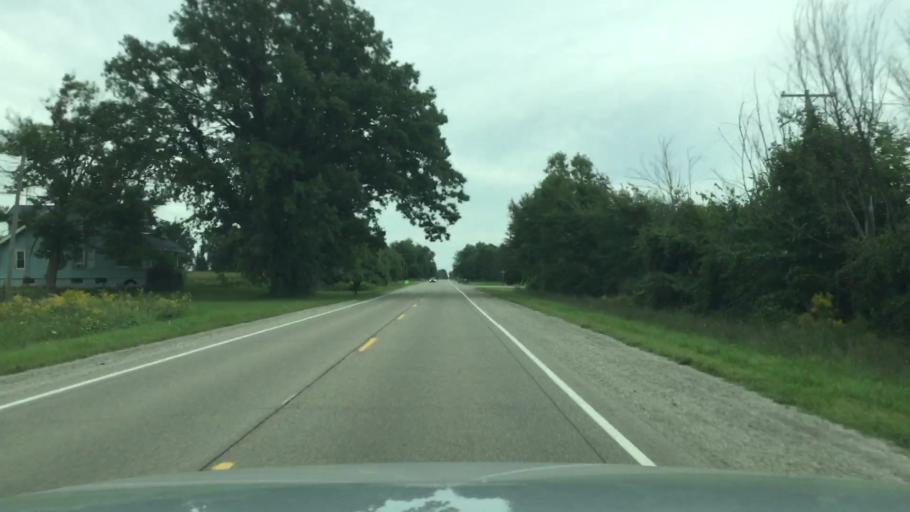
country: US
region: Michigan
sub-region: Genesee County
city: Swartz Creek
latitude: 42.9570
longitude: -83.8935
